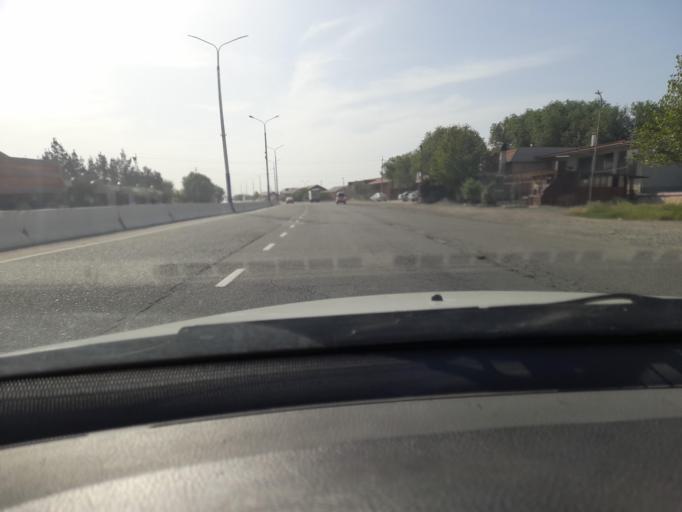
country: UZ
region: Samarqand
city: Kattaqo'rg'on
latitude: 39.9227
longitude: 66.2859
